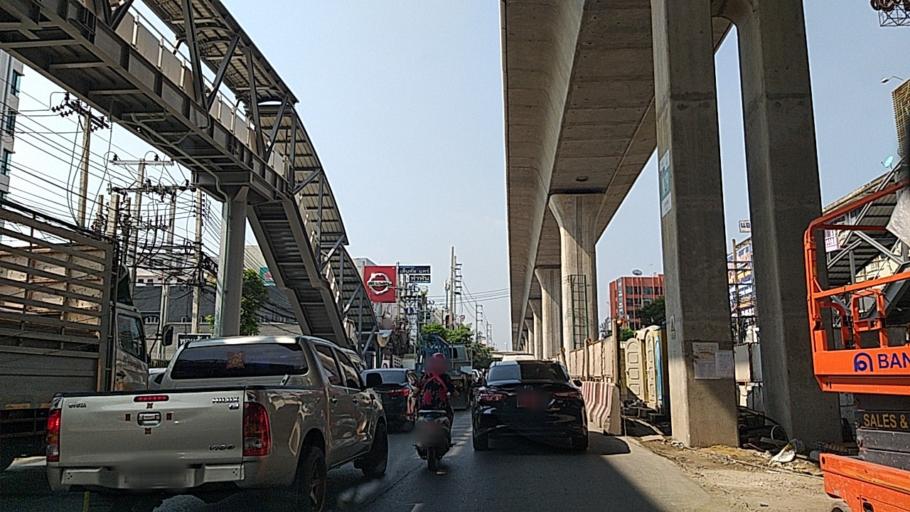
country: TH
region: Bangkok
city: Bang Khen
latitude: 13.8879
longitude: 100.6041
